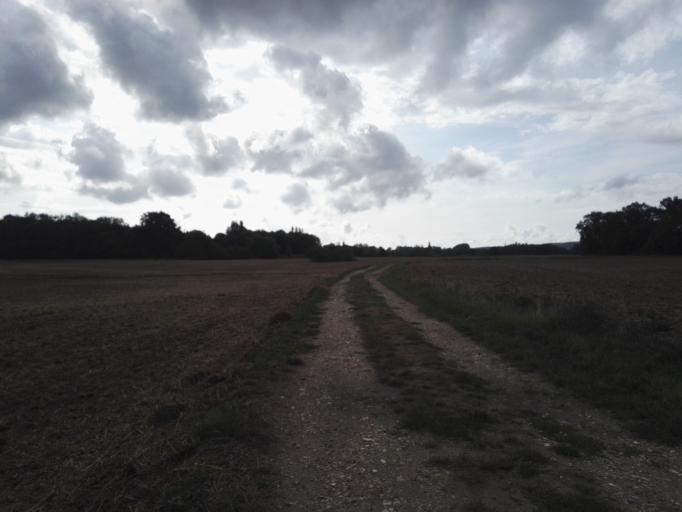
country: FR
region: Haute-Normandie
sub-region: Departement de l'Eure
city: Houlbec-Cocherel
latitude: 49.0643
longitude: 1.3078
